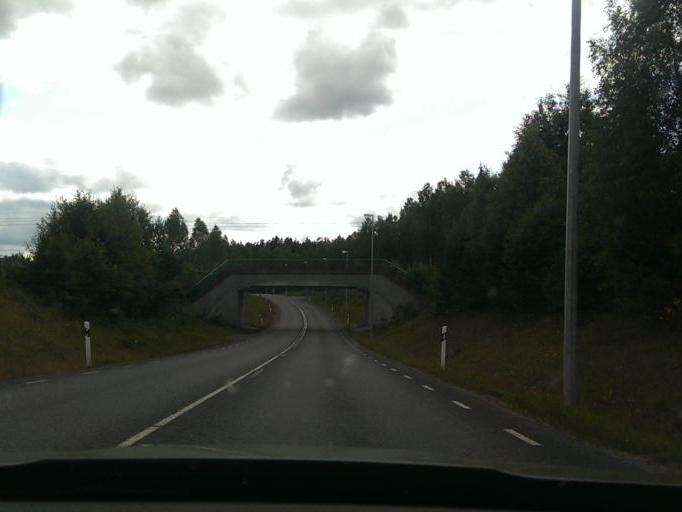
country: SE
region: Joenkoeping
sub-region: Varnamo Kommun
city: Varnamo
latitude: 57.2061
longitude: 14.0289
